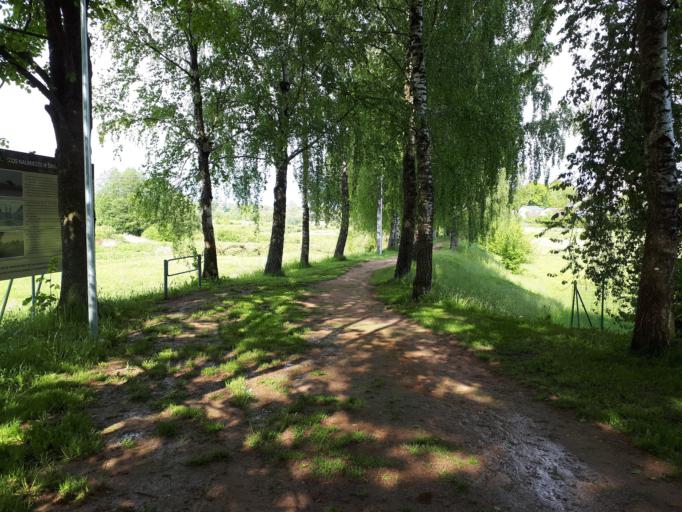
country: LT
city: Kudirkos Naumiestis
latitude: 54.7750
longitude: 22.8558
